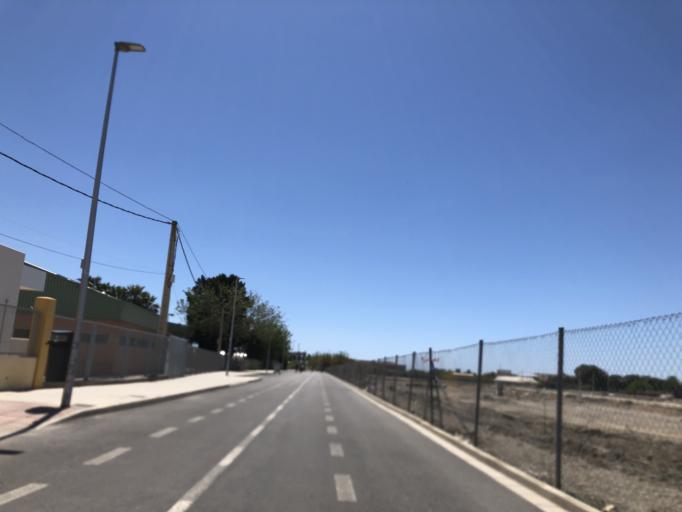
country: ES
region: Andalusia
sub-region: Provincia de Almeria
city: Almeria
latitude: 36.8373
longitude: -2.4051
